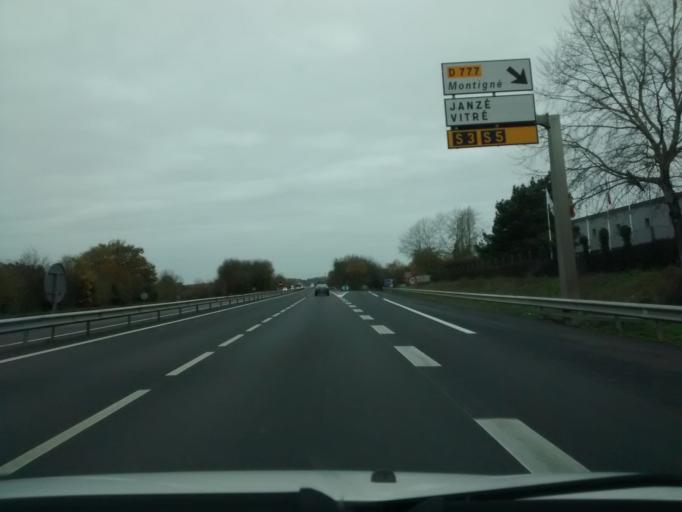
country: FR
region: Brittany
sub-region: Departement d'Ille-et-Vilaine
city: Torce
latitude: 48.0752
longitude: -1.2646
